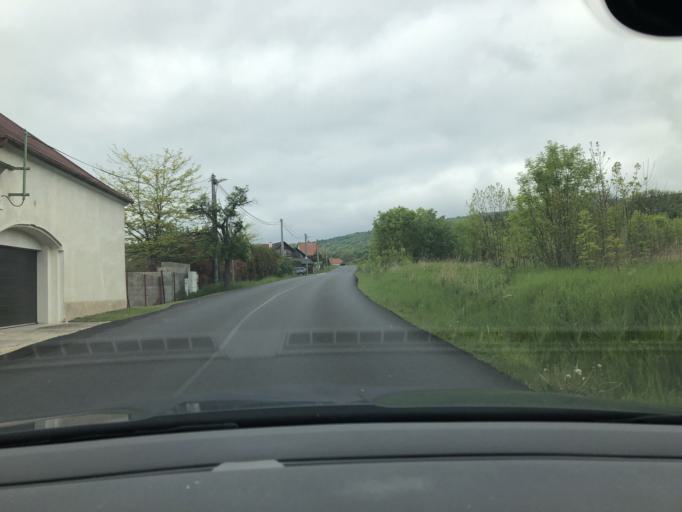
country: CZ
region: Ustecky
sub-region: Okres Usti nad Labem
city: Usti nad Labem
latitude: 50.7014
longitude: 14.0168
